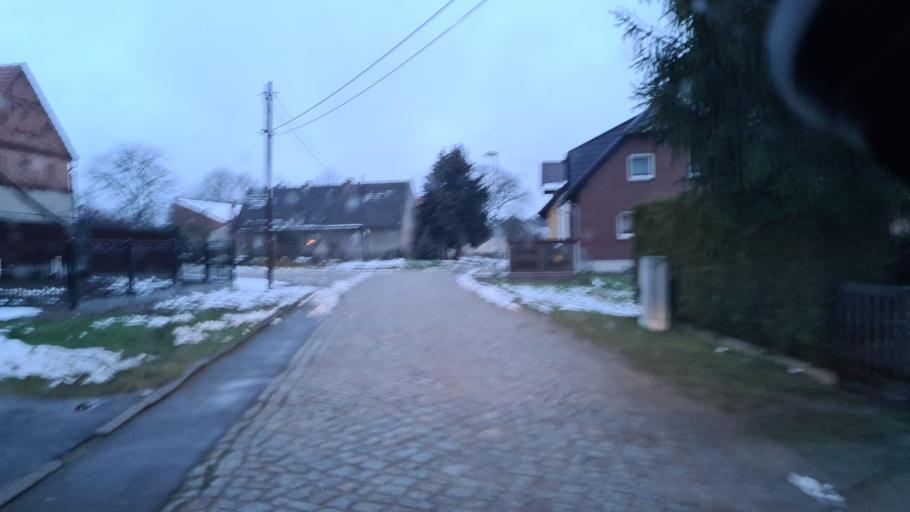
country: DE
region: Brandenburg
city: Schenkendobern
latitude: 51.9085
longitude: 14.5772
